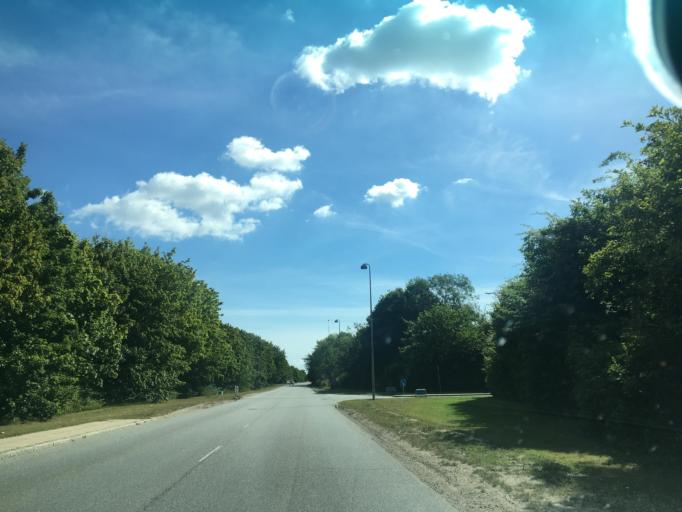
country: DK
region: Zealand
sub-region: Solrod Kommune
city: Solrod Strand
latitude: 55.5744
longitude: 12.2370
